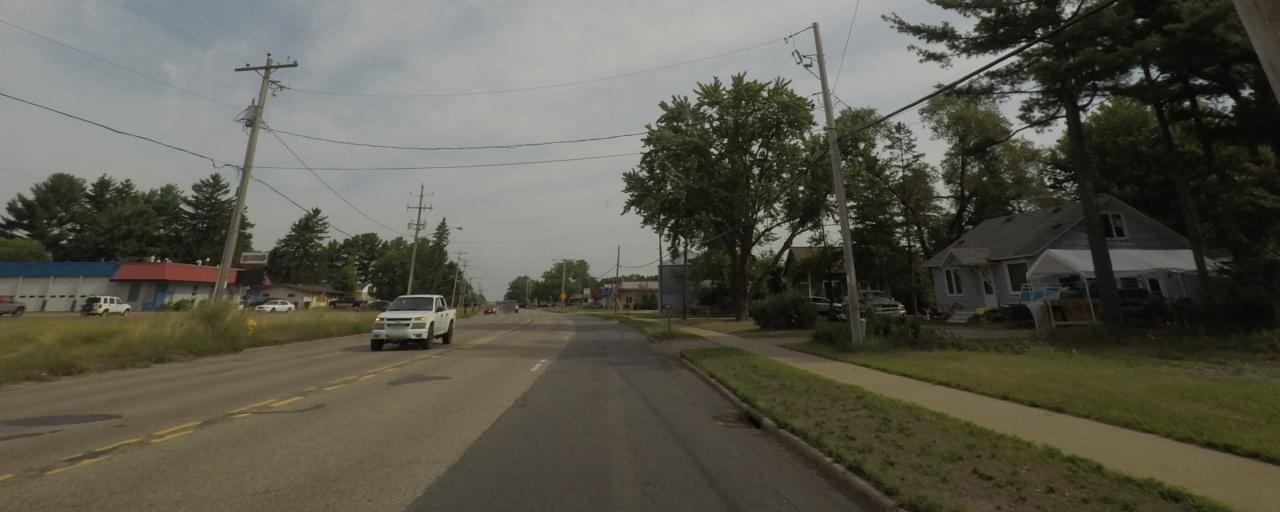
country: US
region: Wisconsin
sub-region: Portage County
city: Plover
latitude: 44.4747
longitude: -89.5476
